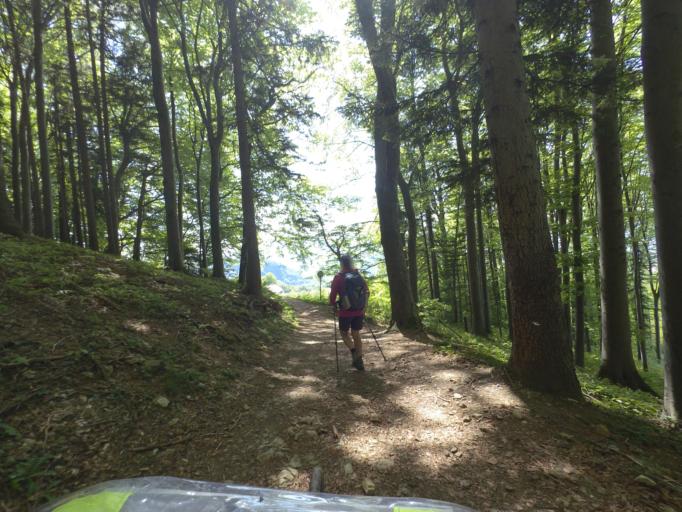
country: AT
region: Salzburg
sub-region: Politischer Bezirk Salzburg-Umgebung
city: Hallwang
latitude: 47.8257
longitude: 13.0898
